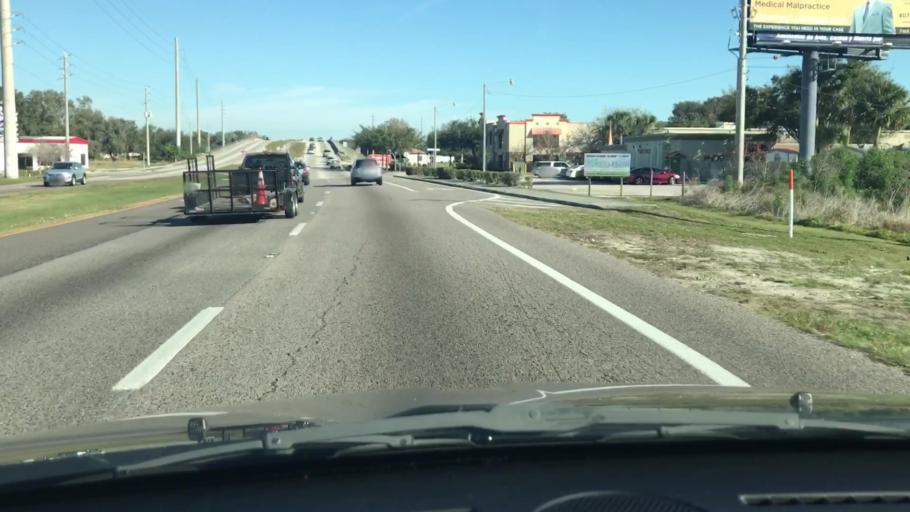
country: US
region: Florida
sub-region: Osceola County
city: Kissimmee
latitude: 28.2816
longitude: -81.4160
